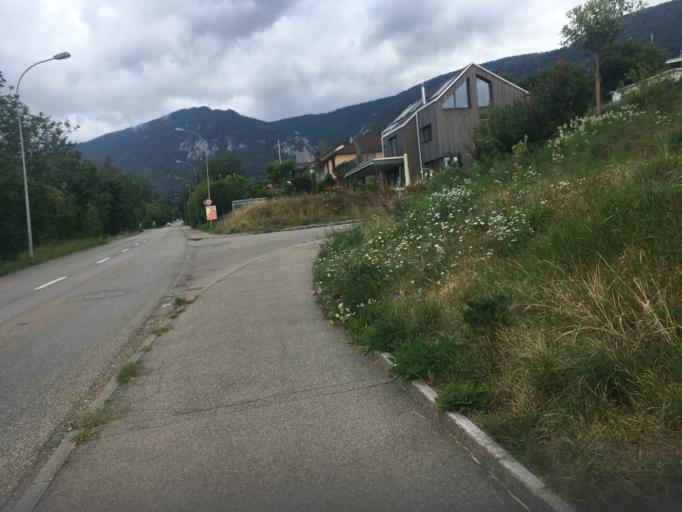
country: CH
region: Solothurn
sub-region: Bezirk Lebern
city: Langendorf
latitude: 47.2264
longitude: 7.5107
